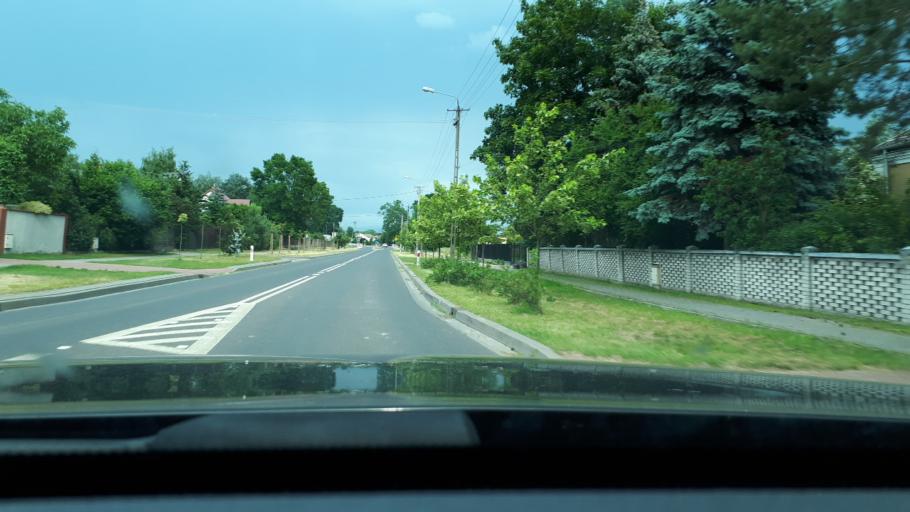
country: PL
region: Masovian Voivodeship
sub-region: Powiat warszawski zachodni
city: Leszno
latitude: 52.2564
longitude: 20.5615
